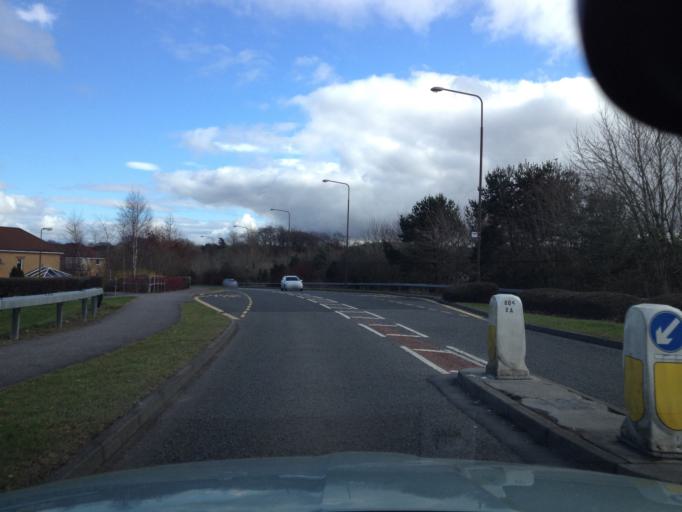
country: GB
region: Scotland
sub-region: West Lothian
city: Livingston
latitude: 55.8694
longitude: -3.5131
